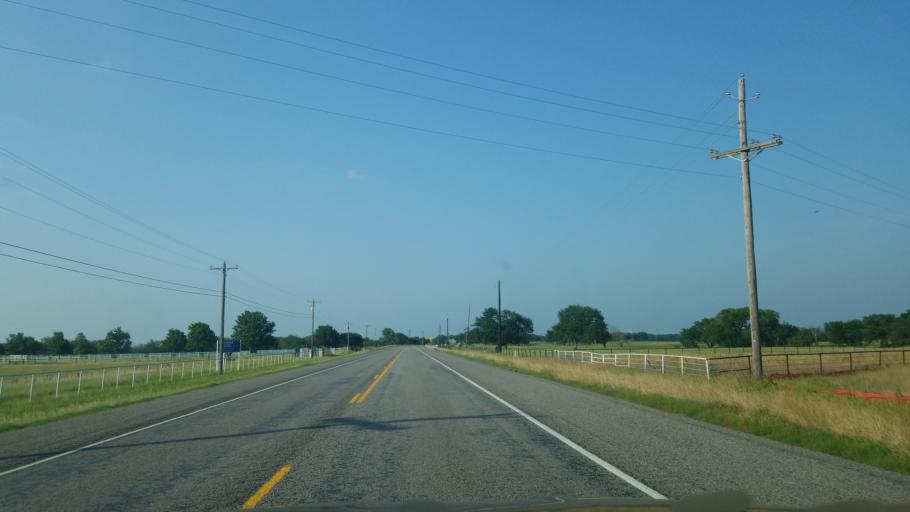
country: US
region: Texas
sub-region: Denton County
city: Denton
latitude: 33.2736
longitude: -97.0982
